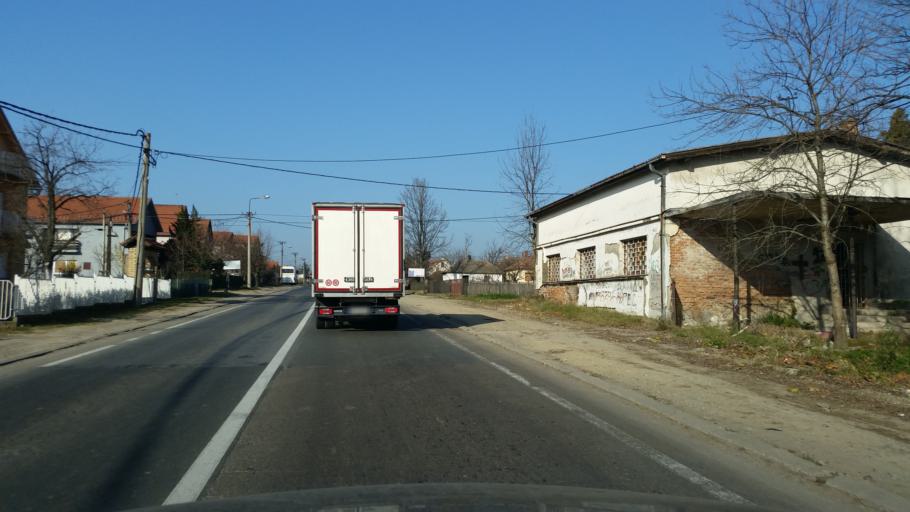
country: RS
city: Stepojevac
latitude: 44.5165
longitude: 20.2936
